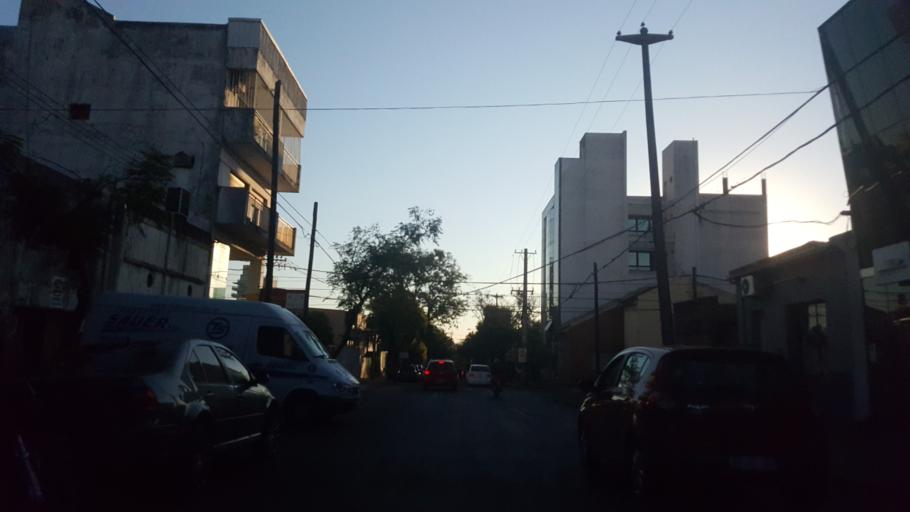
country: AR
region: Misiones
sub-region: Departamento de Capital
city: Posadas
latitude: -27.3646
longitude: -55.8981
